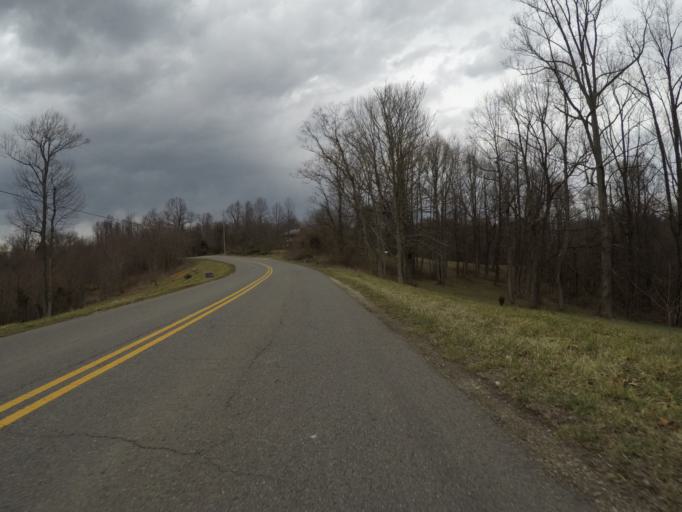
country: US
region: Ohio
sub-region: Lawrence County
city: Burlington
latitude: 38.4371
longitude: -82.5290
